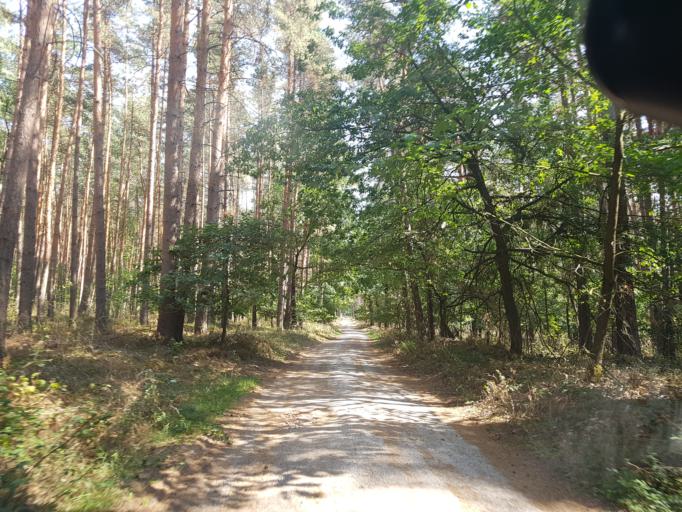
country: DE
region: Saxony-Anhalt
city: Coswig
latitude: 51.9745
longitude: 12.4596
